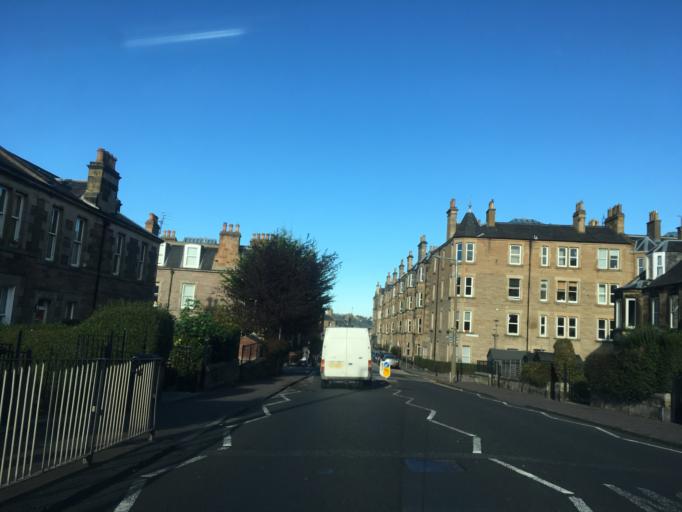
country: GB
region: Scotland
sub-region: Edinburgh
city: Colinton
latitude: 55.9336
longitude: -3.2301
